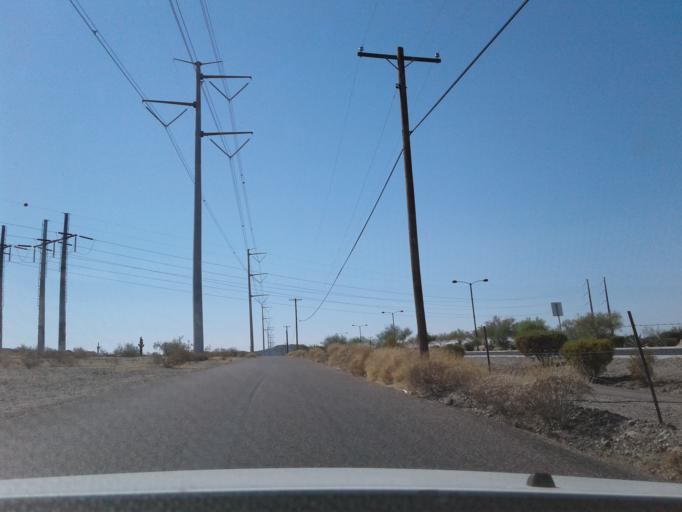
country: US
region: Arizona
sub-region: Maricopa County
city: Laveen
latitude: 33.3222
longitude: -112.1661
